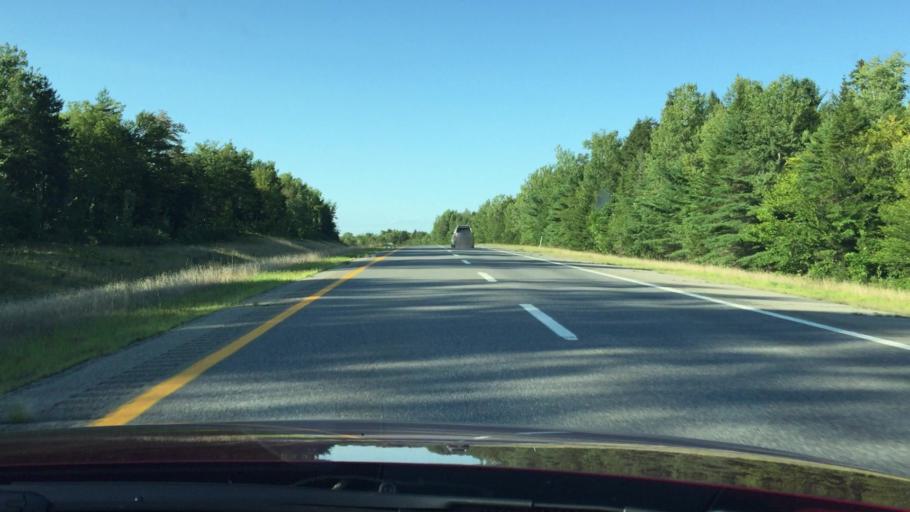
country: US
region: Maine
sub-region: Penobscot County
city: Lincoln
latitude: 45.4203
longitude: -68.5905
